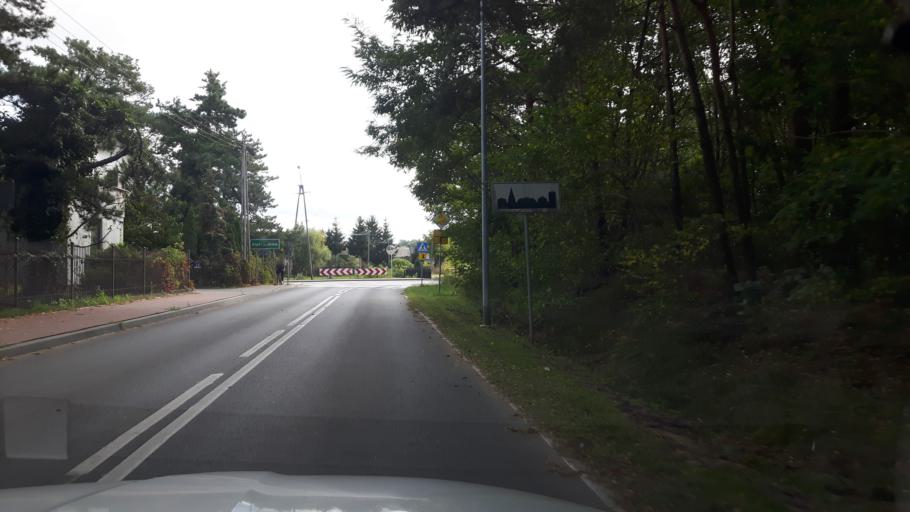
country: PL
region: Masovian Voivodeship
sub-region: Powiat legionowski
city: Stanislawow Pierwszy
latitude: 52.3955
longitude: 21.0563
